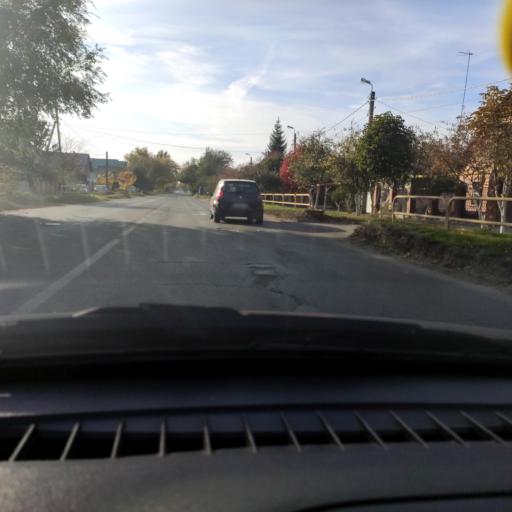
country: RU
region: Samara
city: Tol'yatti
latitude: 53.5383
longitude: 49.4162
